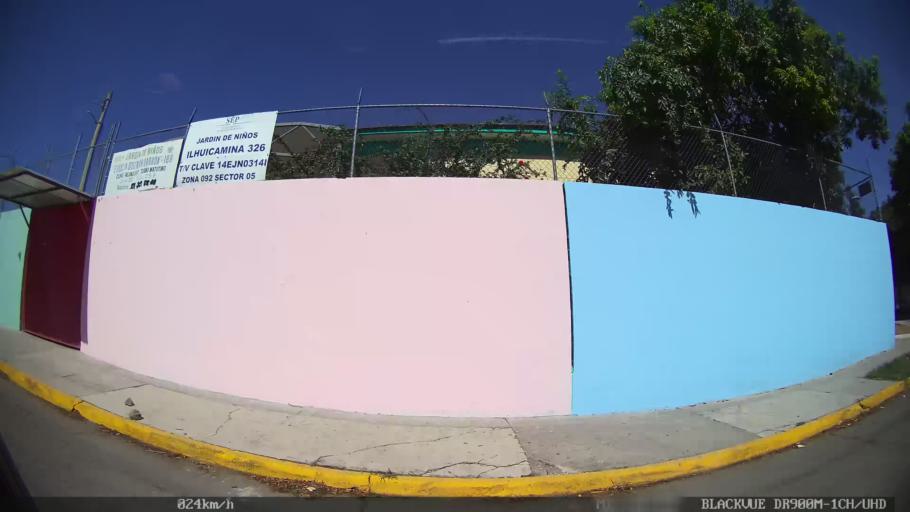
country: MX
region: Jalisco
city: Tlaquepaque
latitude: 20.6467
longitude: -103.2913
